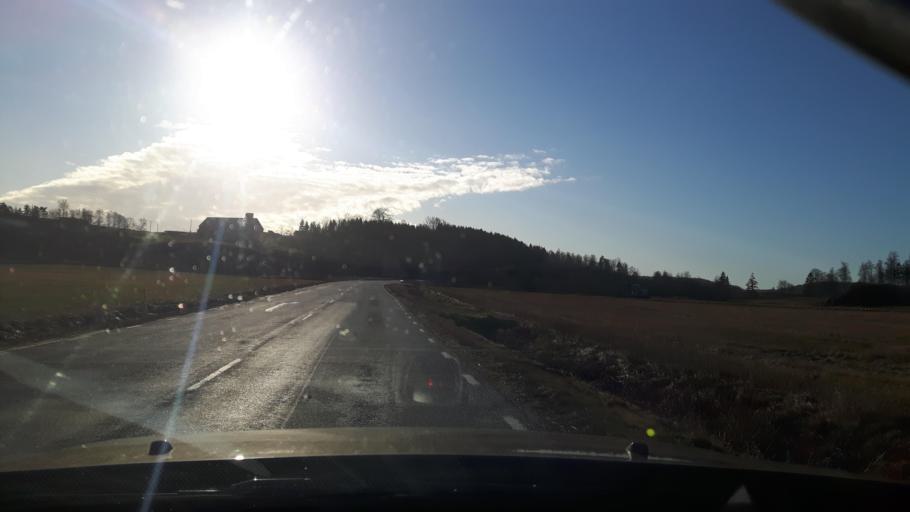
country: SE
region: Vaestra Goetaland
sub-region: Munkedals Kommun
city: Munkedal
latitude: 58.6255
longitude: 11.7712
